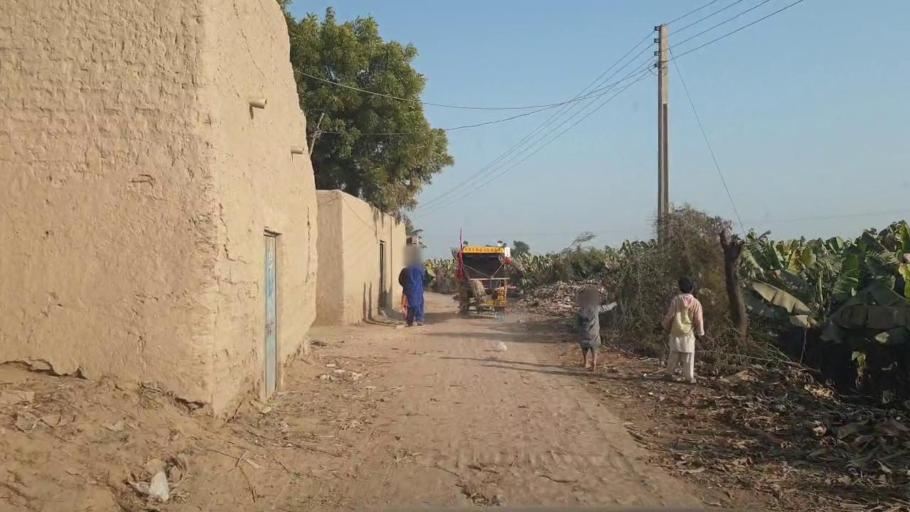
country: PK
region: Sindh
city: Bhit Shah
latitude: 25.8238
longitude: 68.5147
